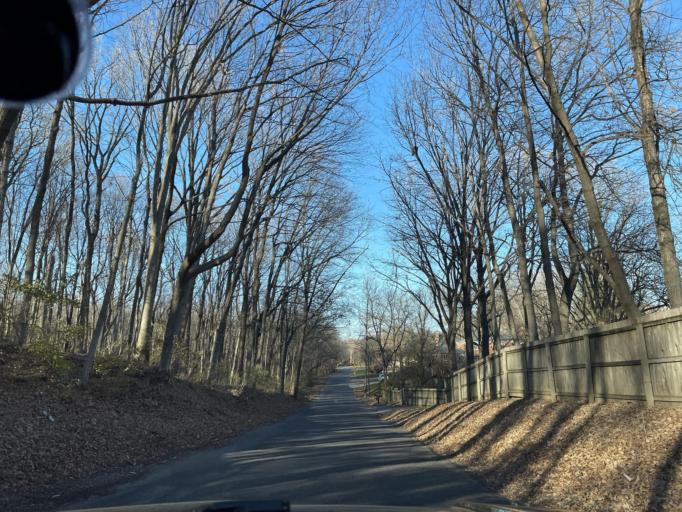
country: US
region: Illinois
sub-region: Sangamon County
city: Leland Grove
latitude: 39.7978
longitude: -89.7155
